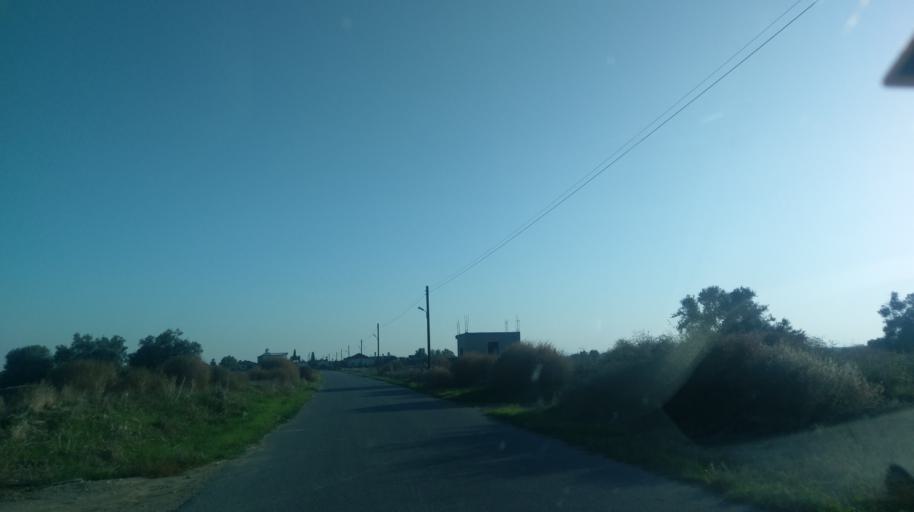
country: CY
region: Ammochostos
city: Lefkonoiko
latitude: 35.2739
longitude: 33.6579
